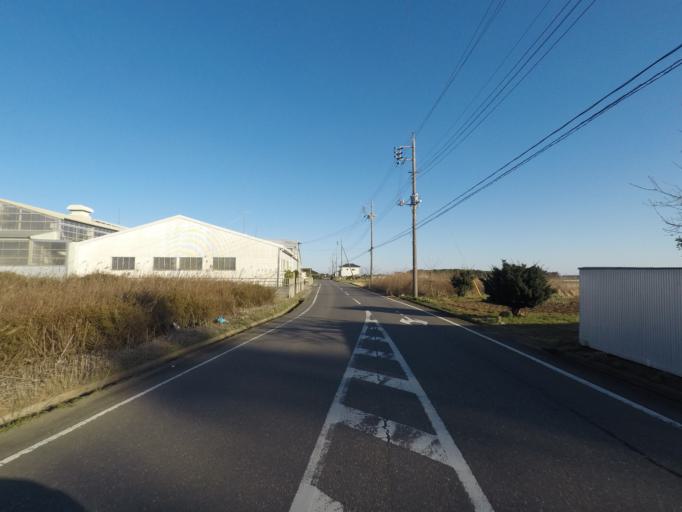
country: JP
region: Ibaraki
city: Ishige
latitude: 36.1331
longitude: 140.0196
